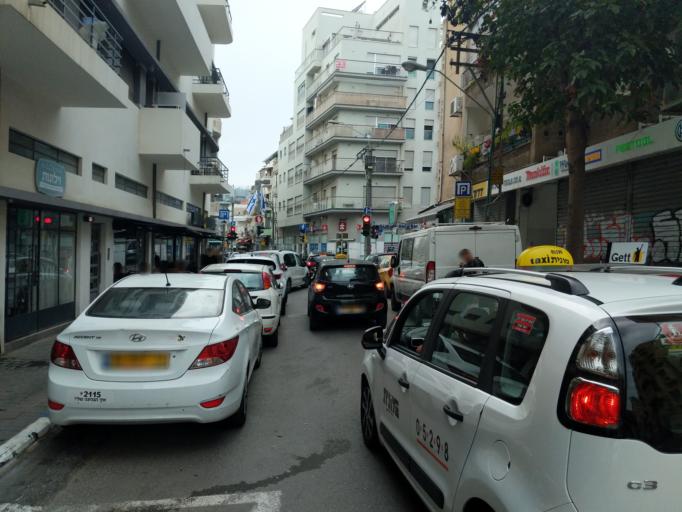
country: IL
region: Tel Aviv
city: Yafo
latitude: 32.0562
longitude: 34.7713
